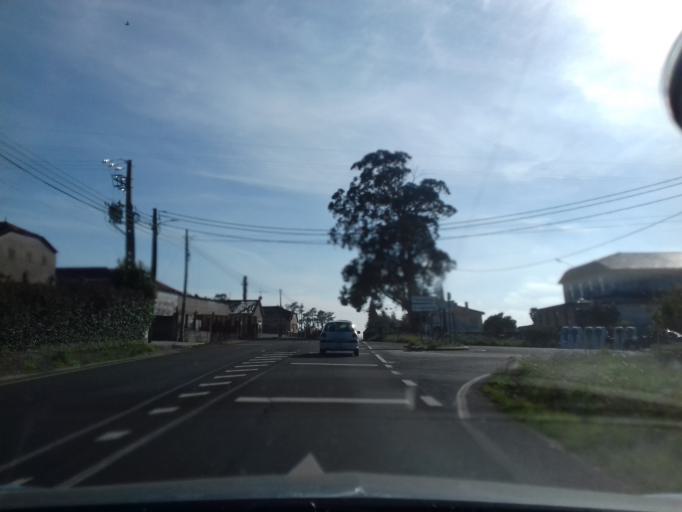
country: PT
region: Leiria
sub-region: Leiria
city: Maceira
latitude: 39.7024
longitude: -8.8708
